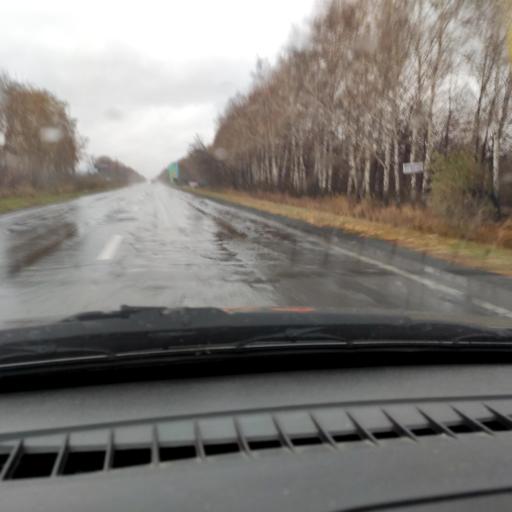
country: RU
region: Samara
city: Tol'yatti
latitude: 53.5952
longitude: 49.3262
